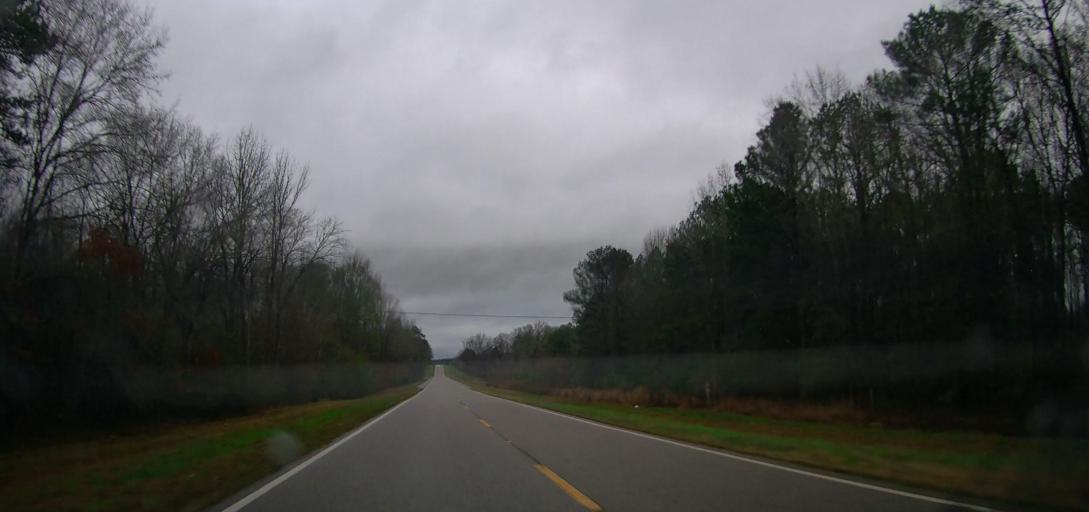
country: US
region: Alabama
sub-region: Bibb County
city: Centreville
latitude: 32.8456
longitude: -86.9598
